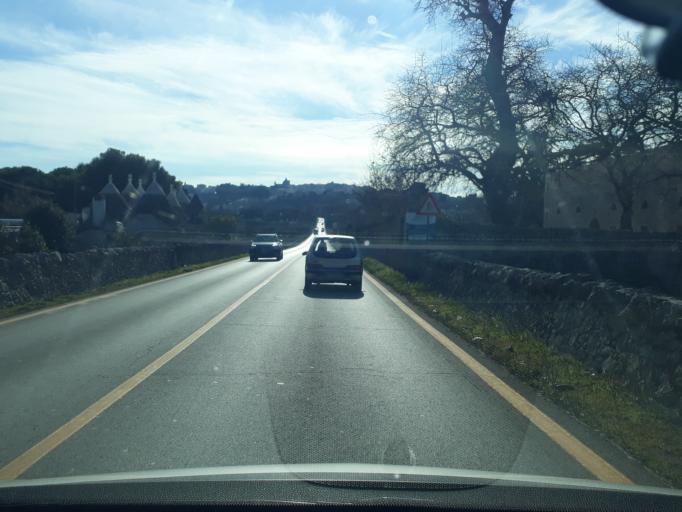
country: IT
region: Apulia
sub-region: Provincia di Taranto
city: Martina Franca
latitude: 40.7213
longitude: 17.3327
